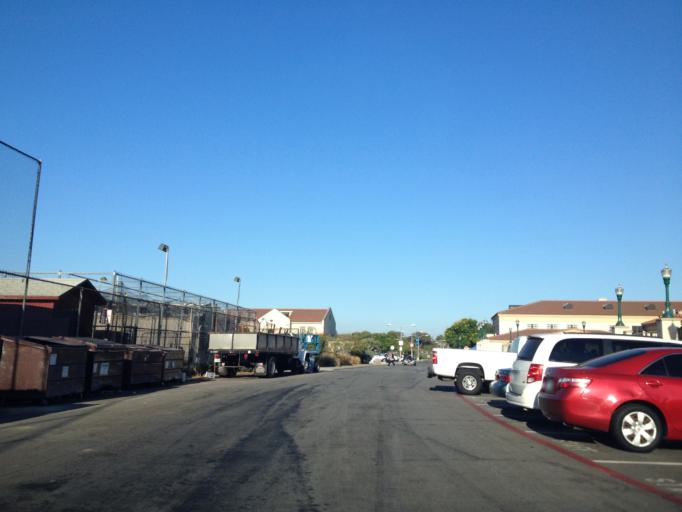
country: US
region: California
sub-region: Orange County
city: Fullerton
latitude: 33.8771
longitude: -117.9184
